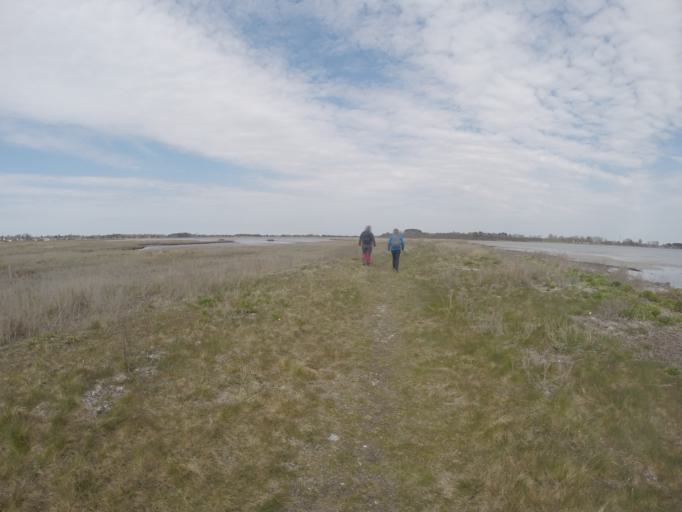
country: DK
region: Zealand
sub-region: Kalundborg Kommune
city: Gorlev
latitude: 55.5215
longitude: 11.1215
